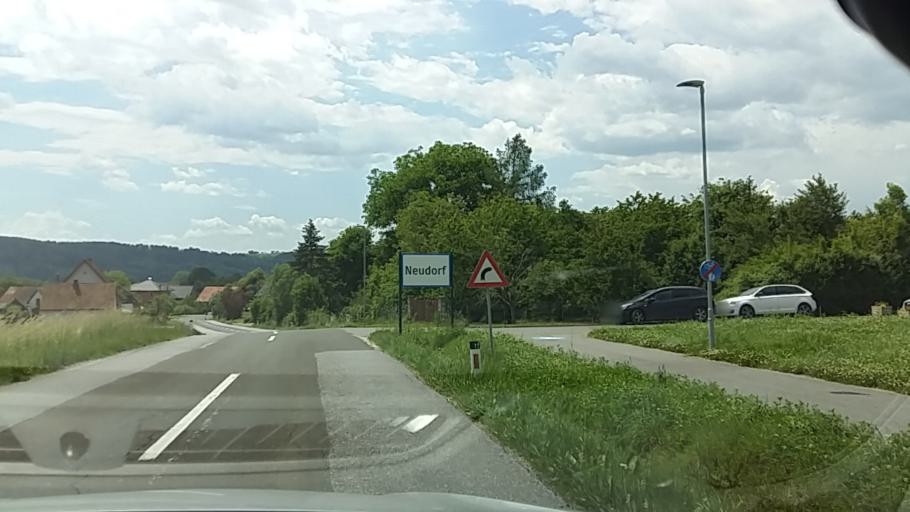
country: AT
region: Styria
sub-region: Politischer Bezirk Hartberg-Fuerstenfeld
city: Hainersdorf
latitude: 47.0895
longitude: 15.9463
